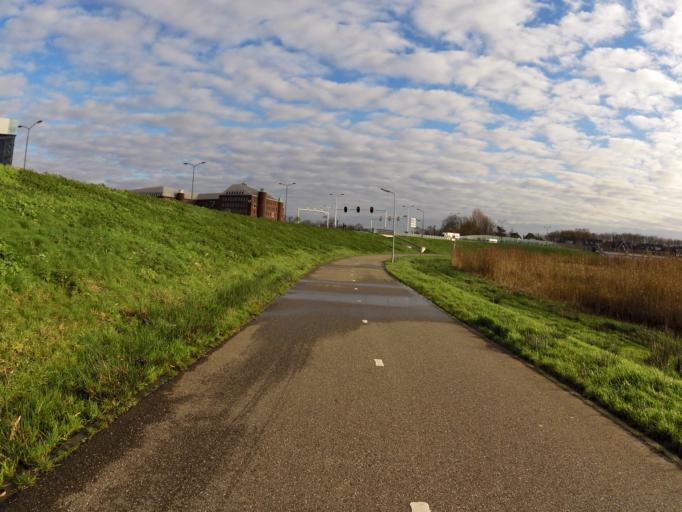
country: NL
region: North Brabant
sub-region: Gemeente 's-Hertogenbosch
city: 's-Hertogenbosch
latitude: 51.6823
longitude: 5.2870
